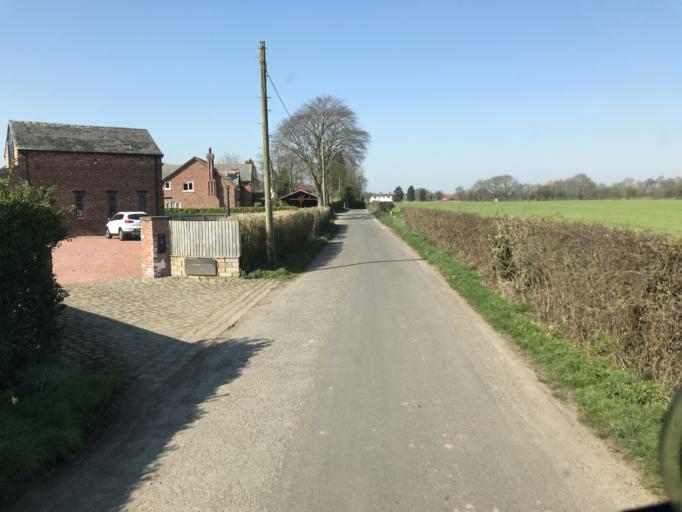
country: GB
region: England
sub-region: Warrington
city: Lymm
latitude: 53.4230
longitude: -2.4709
